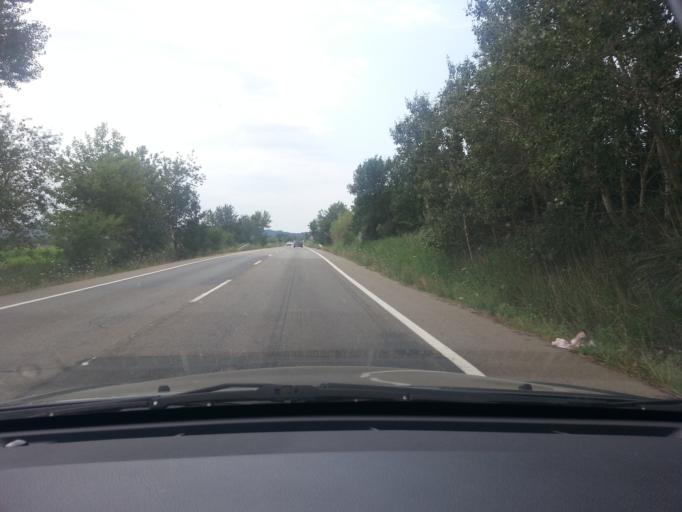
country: ES
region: Catalonia
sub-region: Provincia de Girona
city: Torroella de Montgri
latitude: 42.0107
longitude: 3.1442
